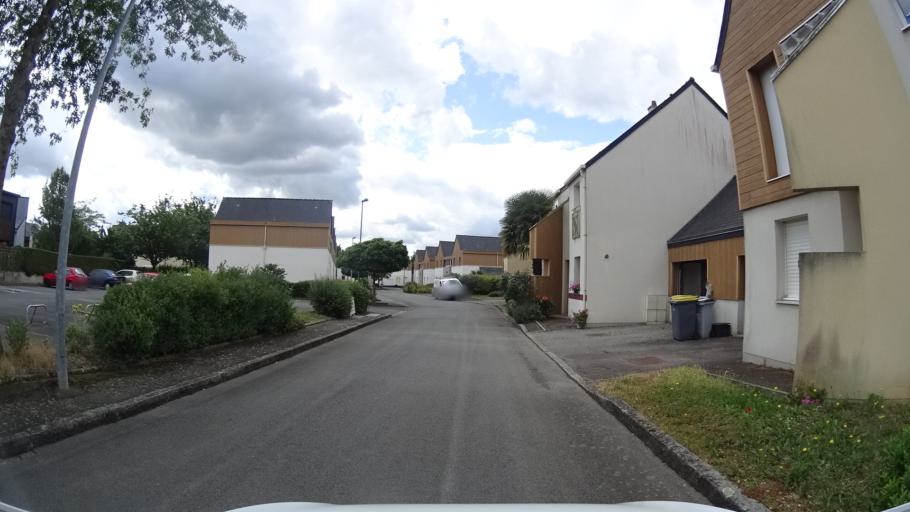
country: FR
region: Brittany
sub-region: Departement d'Ille-et-Vilaine
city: Chartres-de-Bretagne
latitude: 48.0344
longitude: -1.7136
